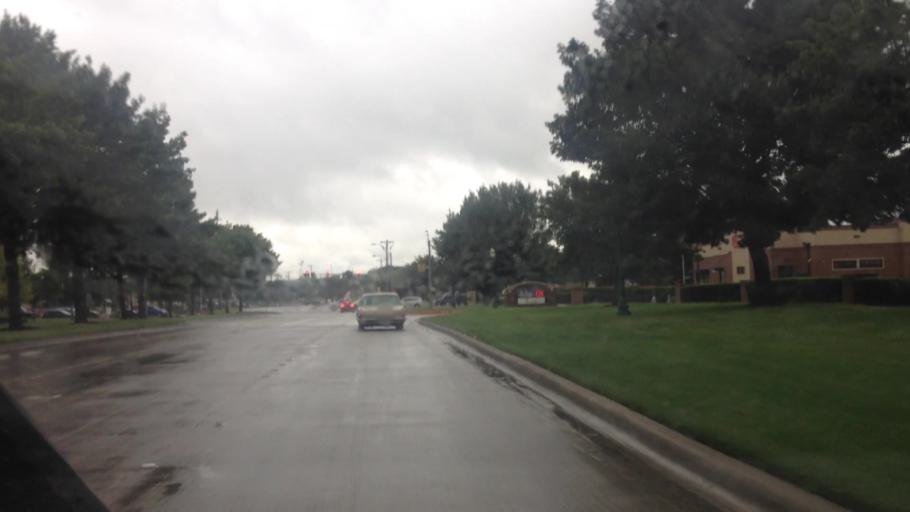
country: US
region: Texas
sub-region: Tarrant County
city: Keller
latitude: 32.9329
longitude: -97.2292
